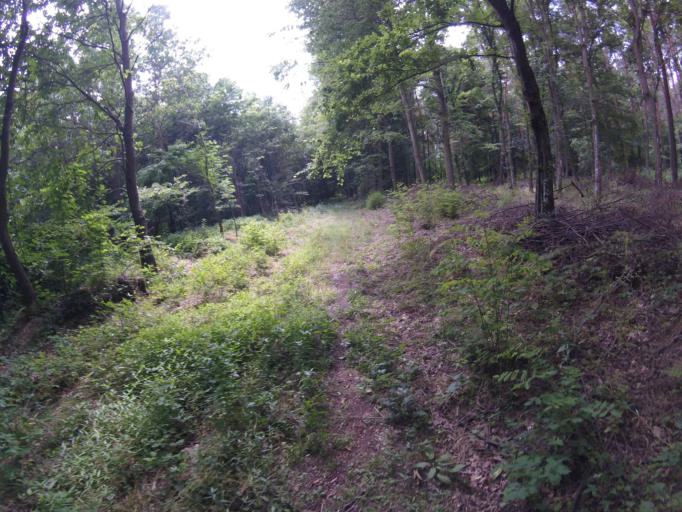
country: HU
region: Zala
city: Turje
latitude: 47.0367
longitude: 17.0727
